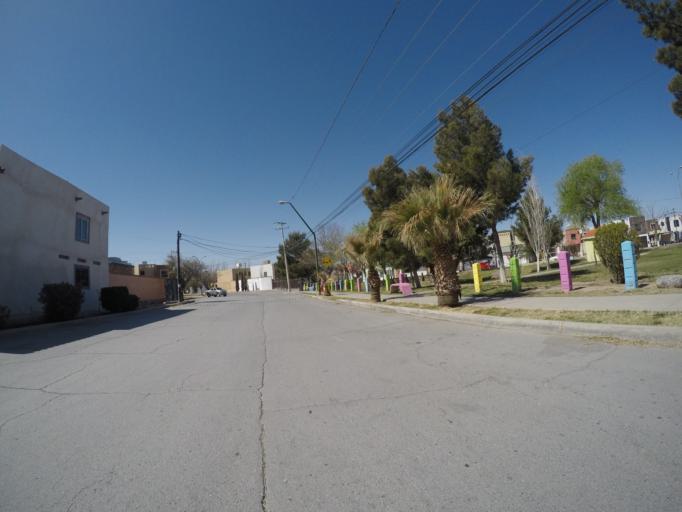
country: MX
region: Chihuahua
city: Ciudad Juarez
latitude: 31.6962
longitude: -106.4146
